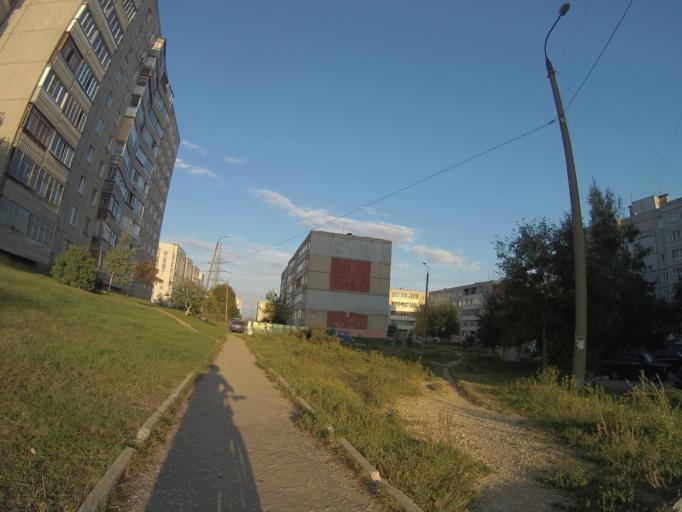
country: RU
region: Vladimir
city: Vladimir
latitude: 56.1028
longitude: 40.3481
